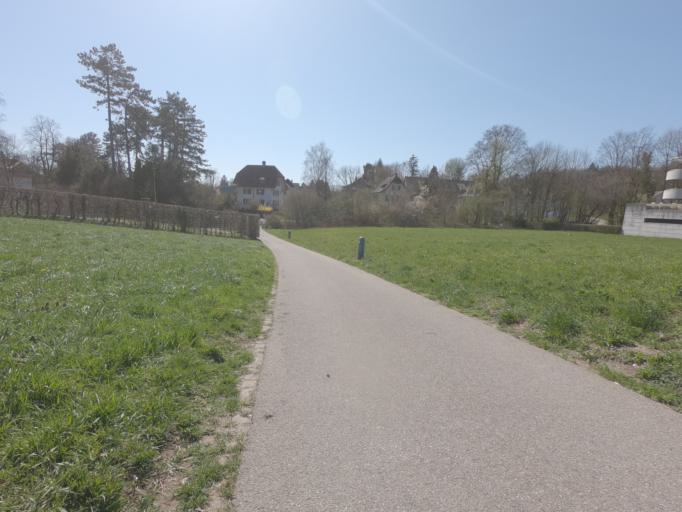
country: CH
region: Solothurn
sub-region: Bezirk Solothurn
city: Solothurn
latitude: 47.2196
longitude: 7.5465
